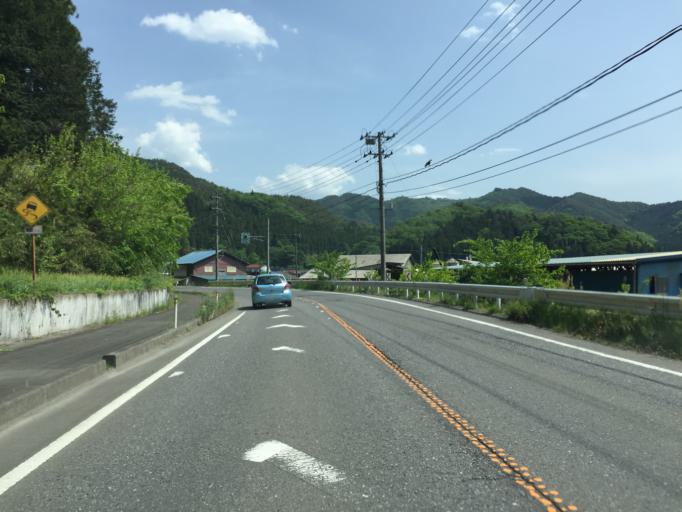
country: JP
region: Fukushima
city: Ishikawa
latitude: 37.0839
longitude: 140.5191
